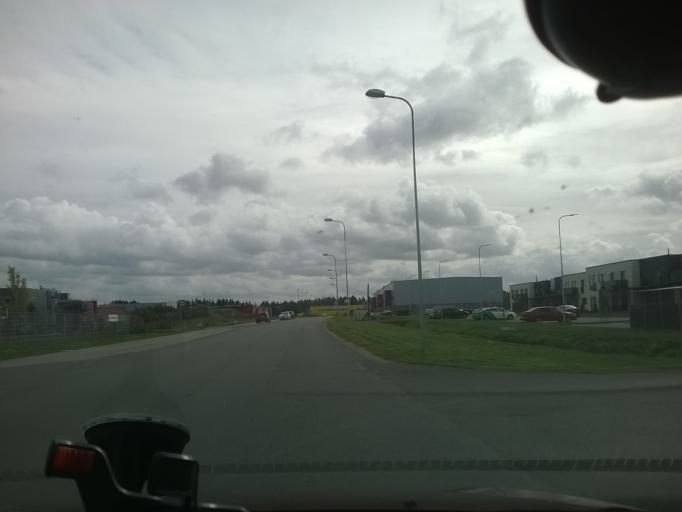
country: EE
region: Harju
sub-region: Rae vald
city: Jueri
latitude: 59.3883
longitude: 24.8237
